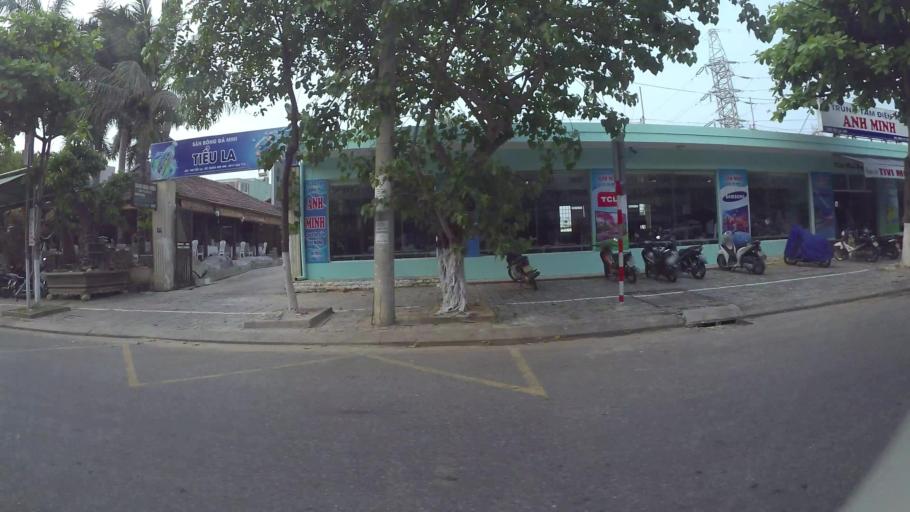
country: VN
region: Da Nang
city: Da Nang
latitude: 16.0444
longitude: 108.2130
